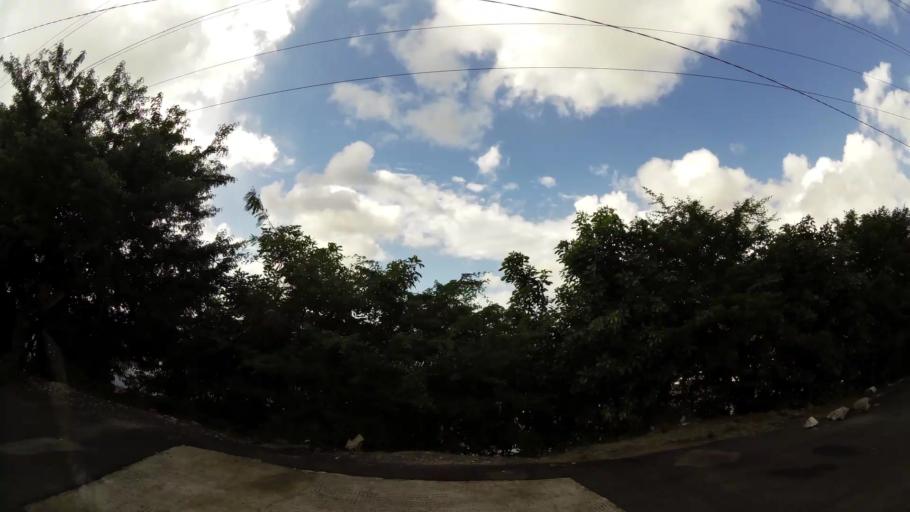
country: MQ
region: Martinique
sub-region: Martinique
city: Fort-de-France
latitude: 14.6017
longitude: -61.0570
